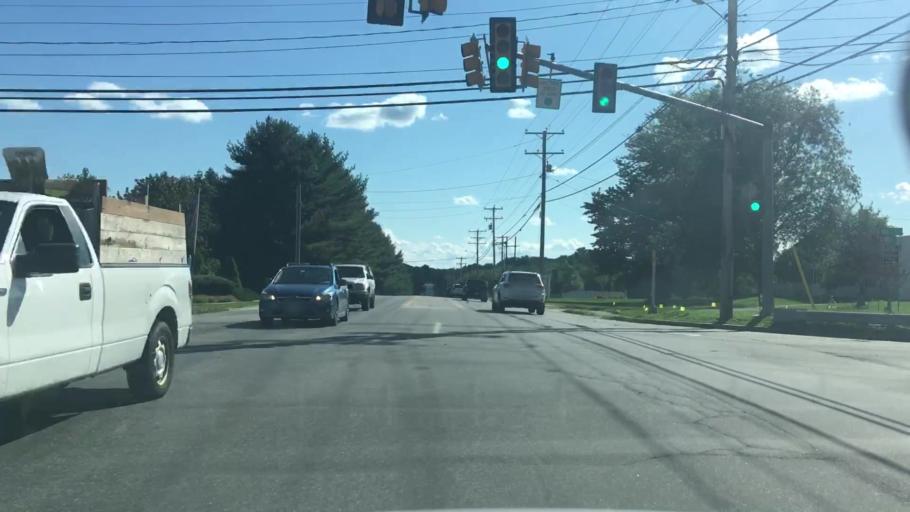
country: US
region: New Hampshire
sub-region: Strafford County
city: Madbury
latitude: 43.1680
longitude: -70.8907
